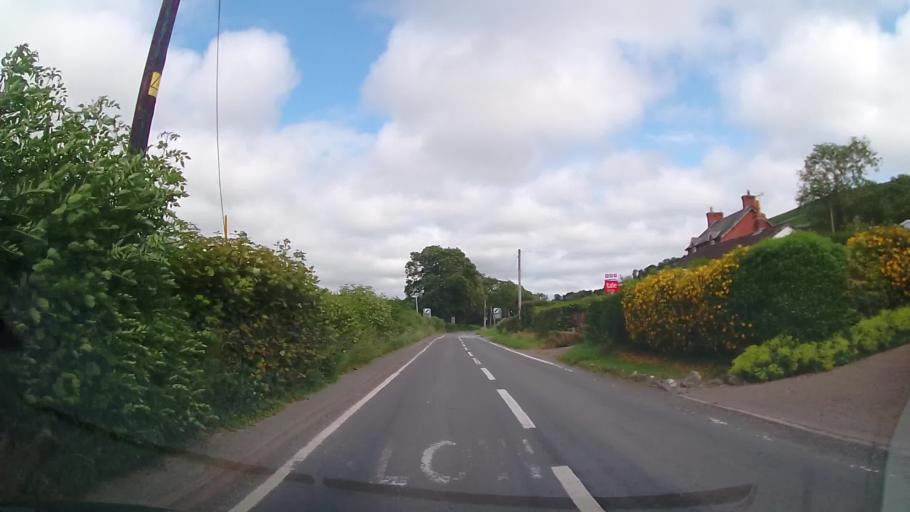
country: GB
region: Wales
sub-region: Sir Powys
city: Llangynog
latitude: 52.8107
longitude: -3.3528
